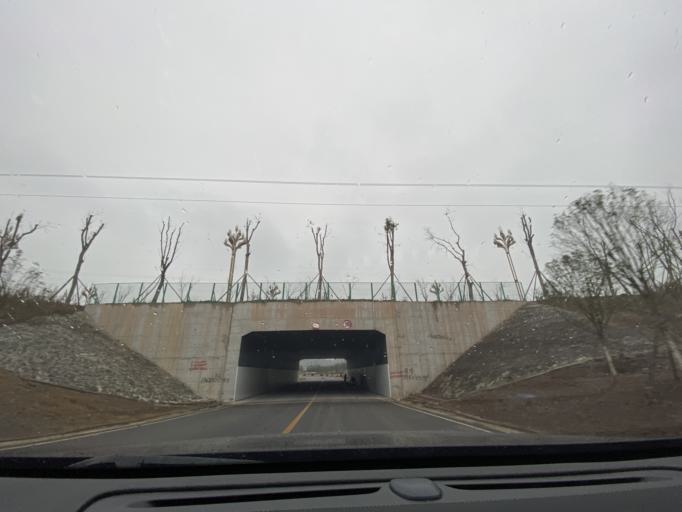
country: CN
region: Sichuan
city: Jiancheng
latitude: 30.3945
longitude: 104.6338
